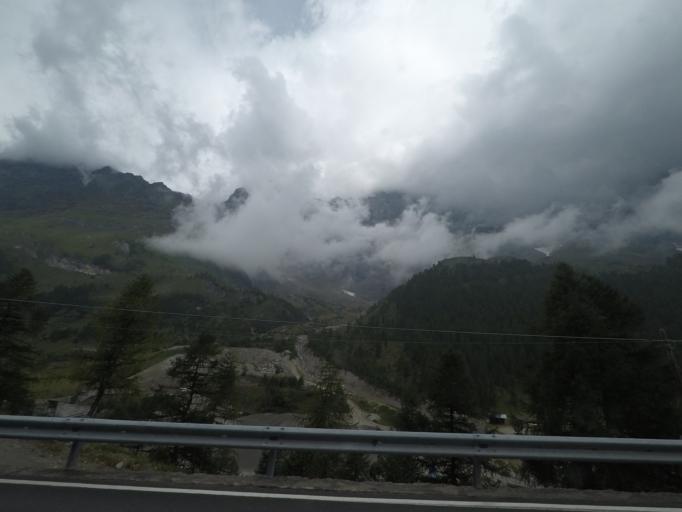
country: IT
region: Aosta Valley
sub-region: Valle d'Aosta
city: Paquier
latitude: 45.9187
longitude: 7.6167
